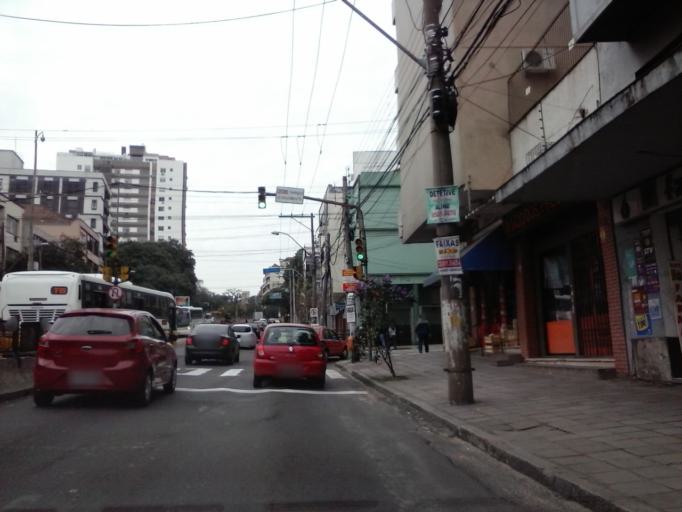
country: BR
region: Rio Grande do Sul
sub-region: Porto Alegre
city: Porto Alegre
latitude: -30.0403
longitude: -51.1962
